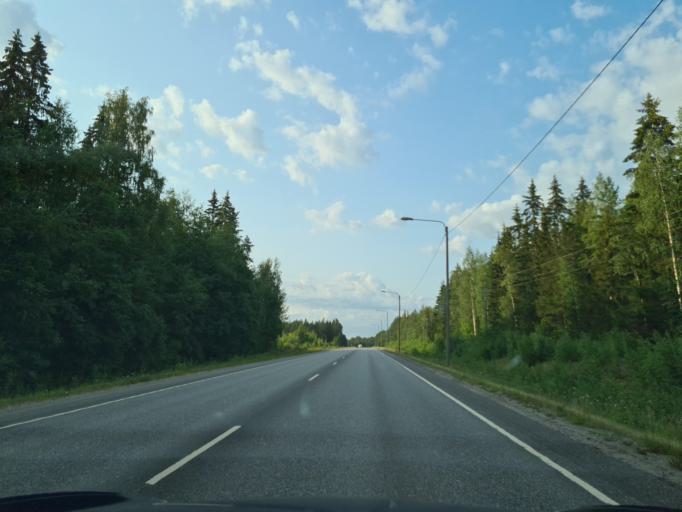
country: FI
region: Southern Ostrobothnia
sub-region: Seinaejoki
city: Lapua
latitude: 63.0114
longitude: 23.0552
